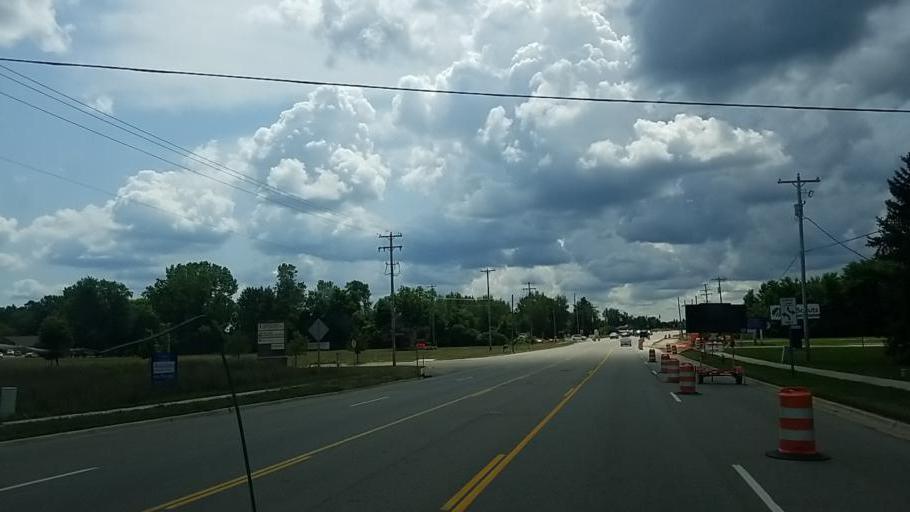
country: US
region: Michigan
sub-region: Kent County
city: Walker
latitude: 43.0243
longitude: -85.7272
